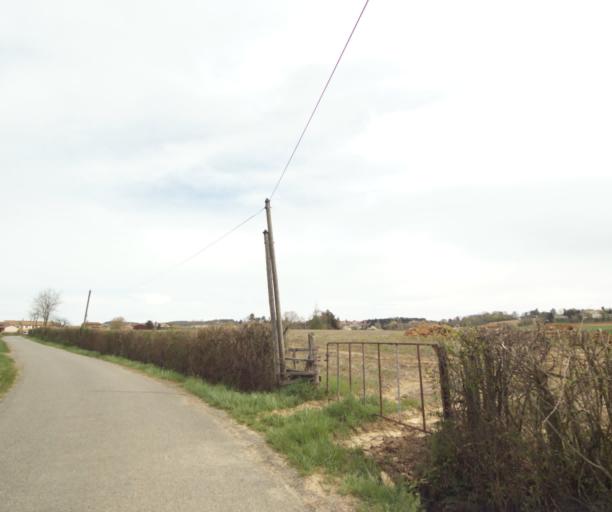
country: FR
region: Bourgogne
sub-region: Departement de Saone-et-Loire
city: Charnay-les-Macon
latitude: 46.3077
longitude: 4.7699
